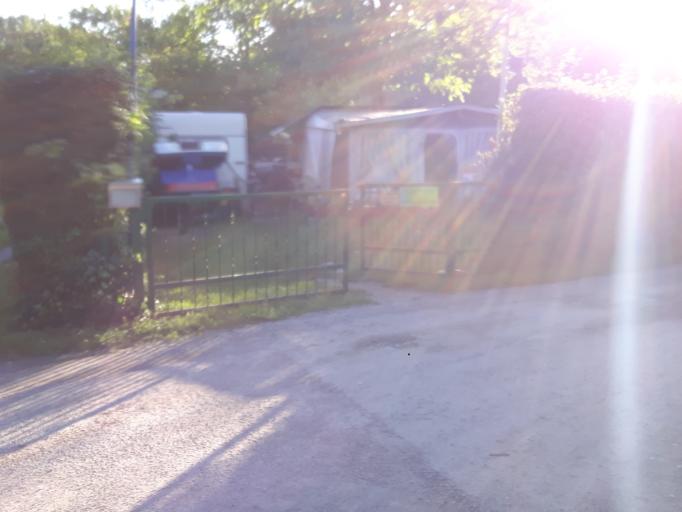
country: DE
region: Rheinland-Pfalz
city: Waldsee
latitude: 49.3962
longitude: 8.4714
